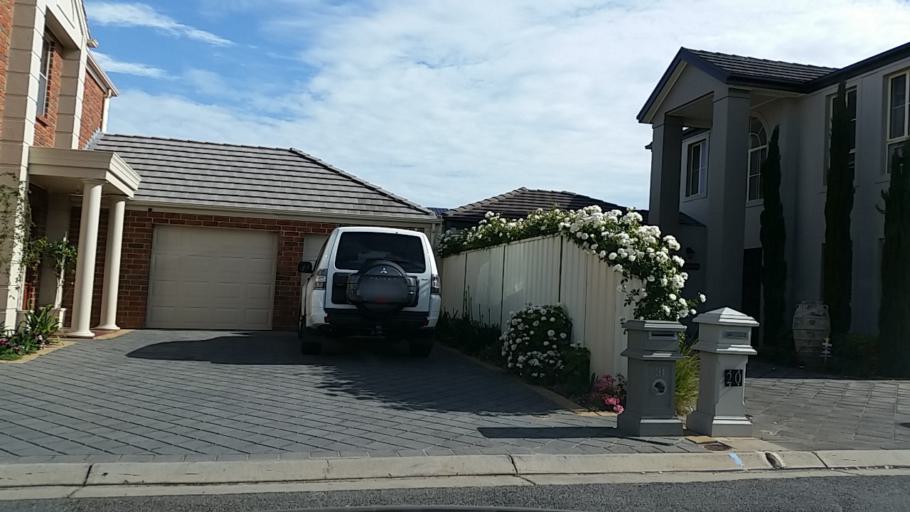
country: AU
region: South Australia
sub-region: Charles Sturt
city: Grange
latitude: -34.8947
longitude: 138.4985
